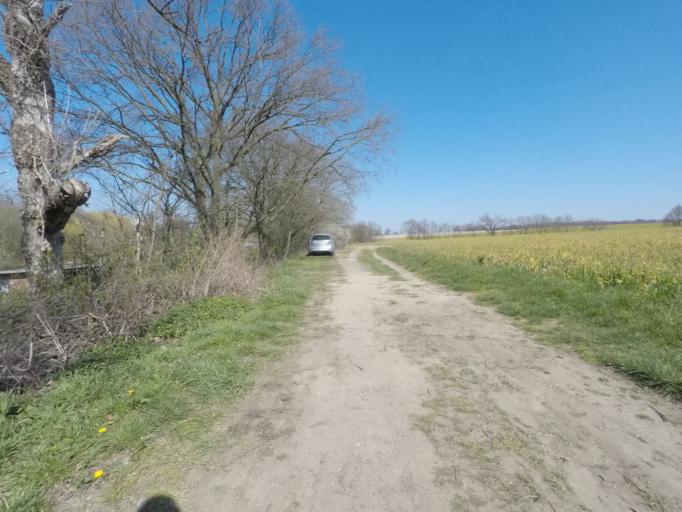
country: DE
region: North Rhine-Westphalia
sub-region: Regierungsbezirk Detmold
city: Herford
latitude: 52.0657
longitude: 8.6177
